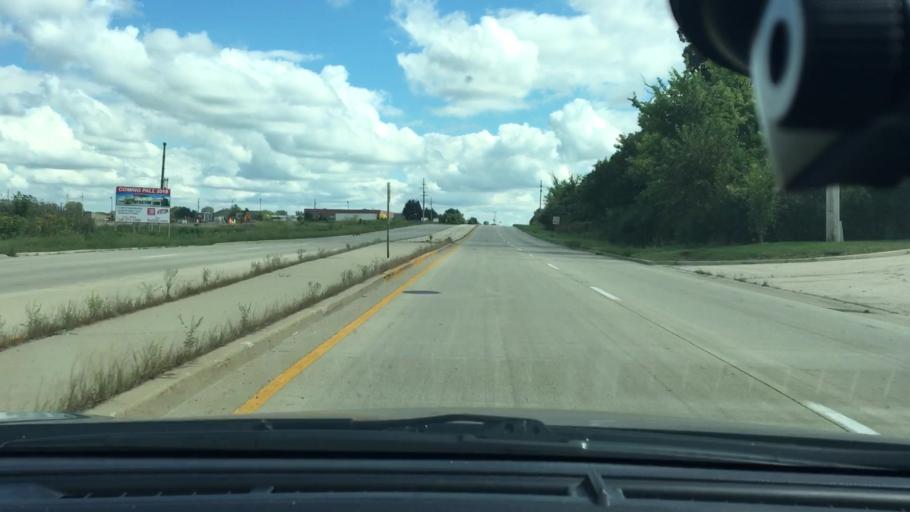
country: US
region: Illinois
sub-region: Kane County
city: East Dundee
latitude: 42.0920
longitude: -88.2546
